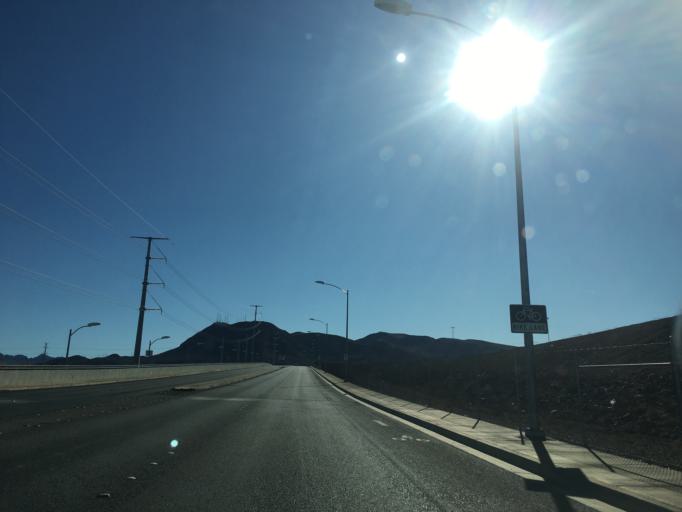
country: US
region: Nevada
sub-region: Clark County
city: Henderson
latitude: 36.0423
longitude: -115.0187
